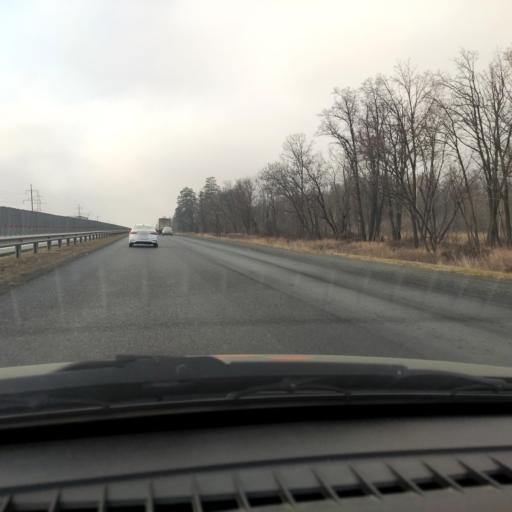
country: RU
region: Samara
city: Pribrezhnyy
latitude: 53.5160
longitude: 49.8703
